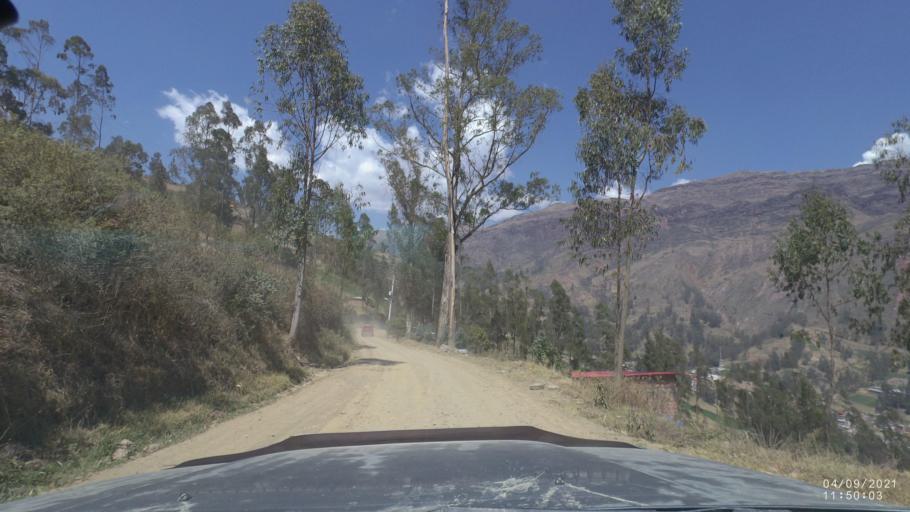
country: BO
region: Cochabamba
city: Colchani
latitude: -17.2249
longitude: -66.5255
